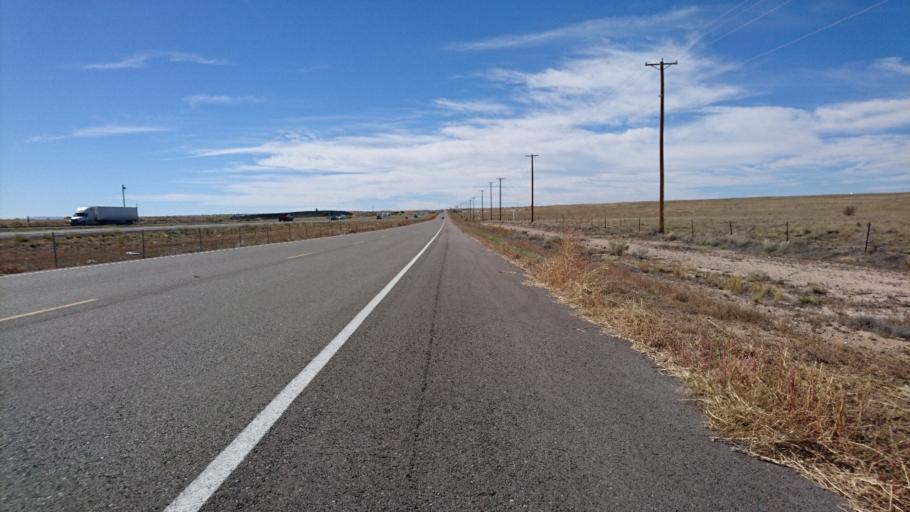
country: US
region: New Mexico
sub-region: Bernalillo County
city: South Valley
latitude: 35.0565
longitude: -106.8298
